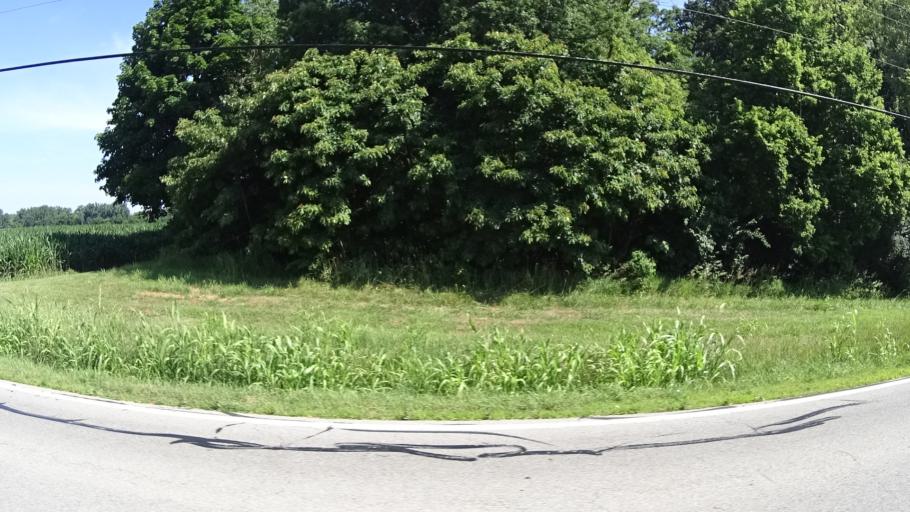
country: US
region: Ohio
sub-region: Huron County
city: Bellevue
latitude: 41.3937
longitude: -82.8176
